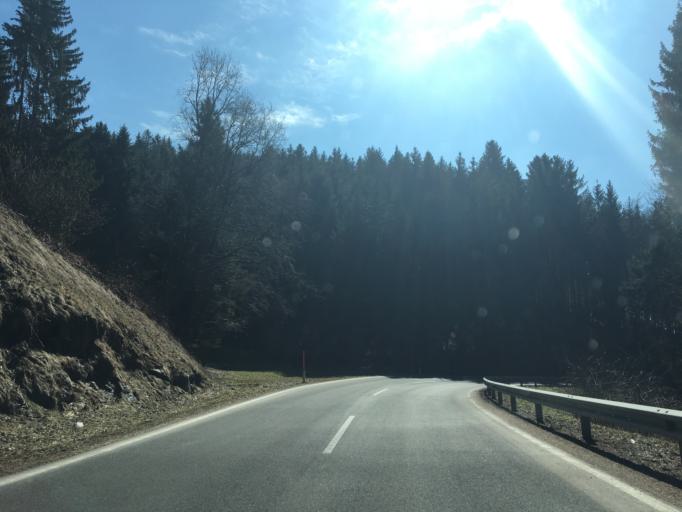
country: AT
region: Upper Austria
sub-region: Politischer Bezirk Perg
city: Sankt Georgen am Walde
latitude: 48.2935
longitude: 14.8984
